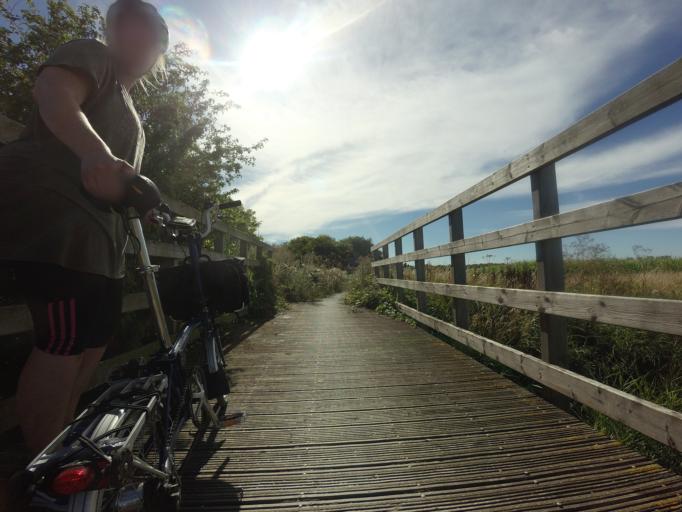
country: GB
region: England
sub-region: Kent
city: Herne Bay
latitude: 51.3643
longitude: 1.2081
